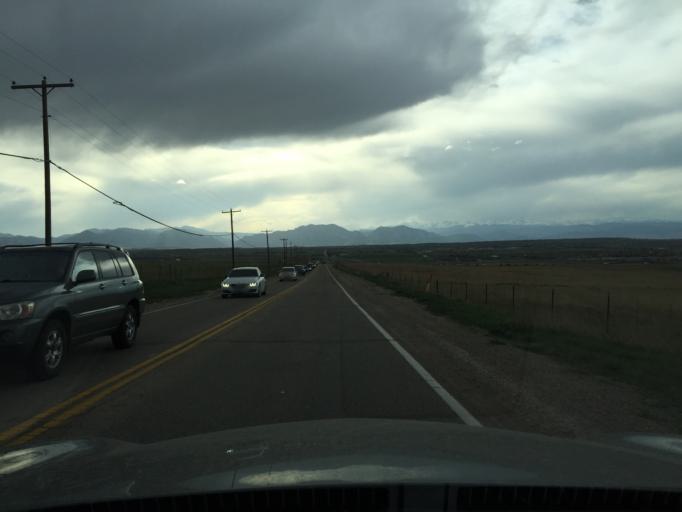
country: US
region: Colorado
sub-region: Broomfield County
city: Broomfield
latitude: 39.9579
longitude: -105.0652
